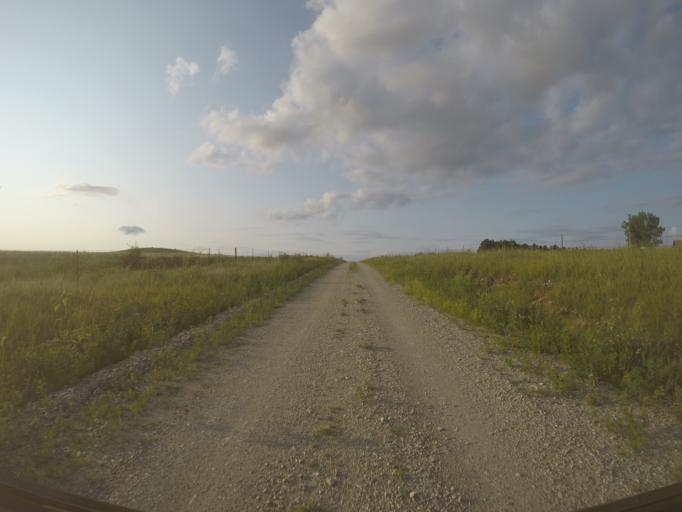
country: US
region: Kansas
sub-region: Wabaunsee County
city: Alma
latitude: 39.0699
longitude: -96.3819
